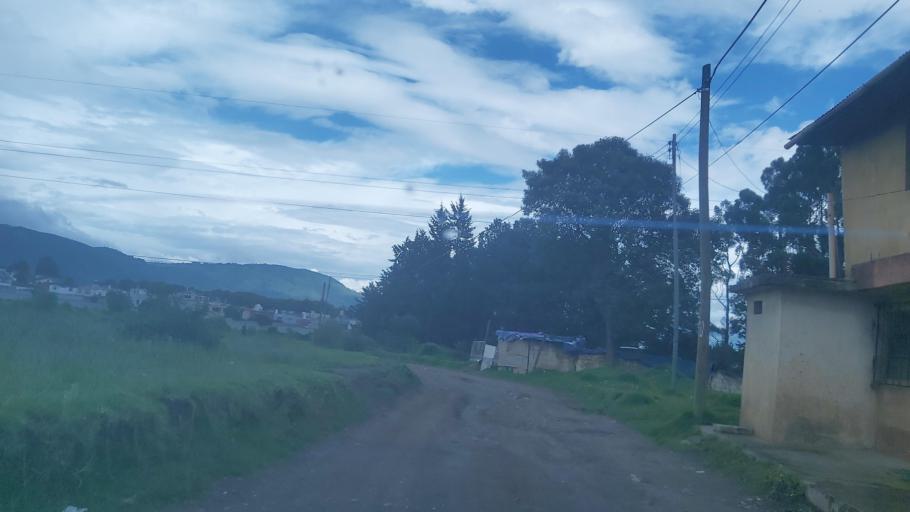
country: GT
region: Quetzaltenango
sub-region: Municipio de La Esperanza
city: La Esperanza
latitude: 14.8519
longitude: -91.5418
